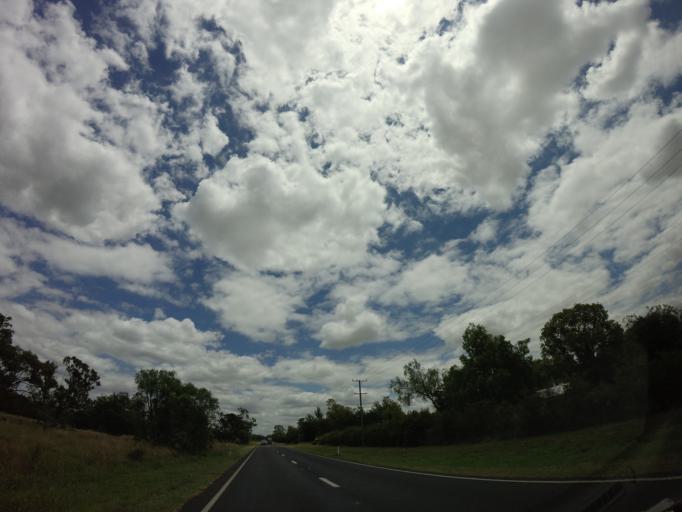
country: AU
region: New South Wales
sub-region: Moree Plains
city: Boggabilla
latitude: -28.5900
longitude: 150.3521
